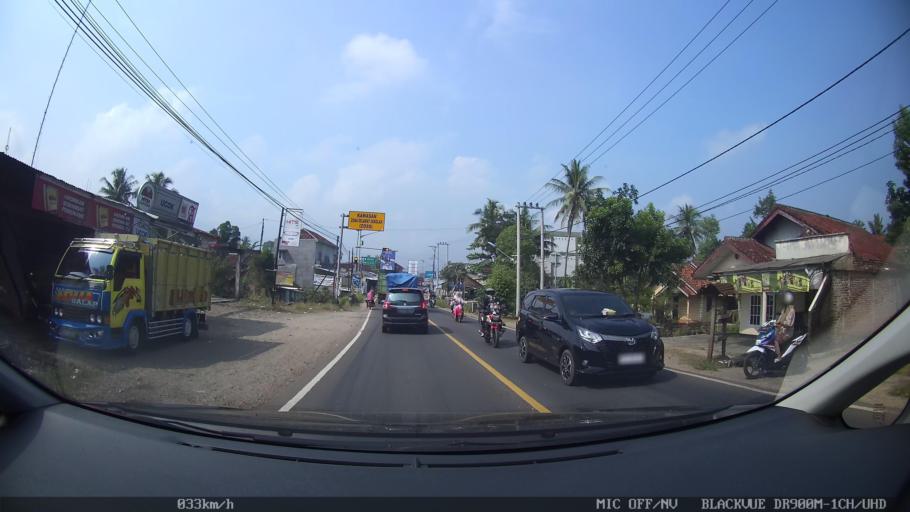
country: ID
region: Lampung
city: Gedongtataan
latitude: -5.3721
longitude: 105.1303
